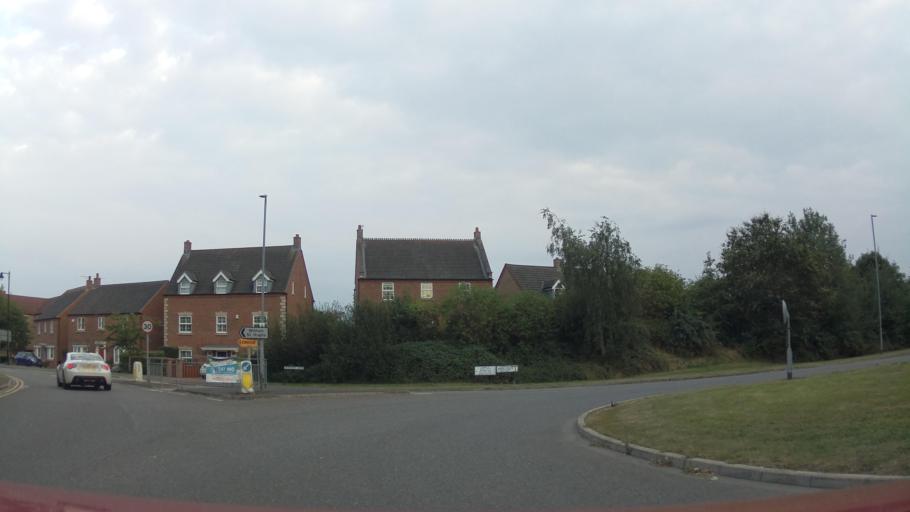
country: GB
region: England
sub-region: Nottinghamshire
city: South Collingham
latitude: 53.1489
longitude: -0.6695
